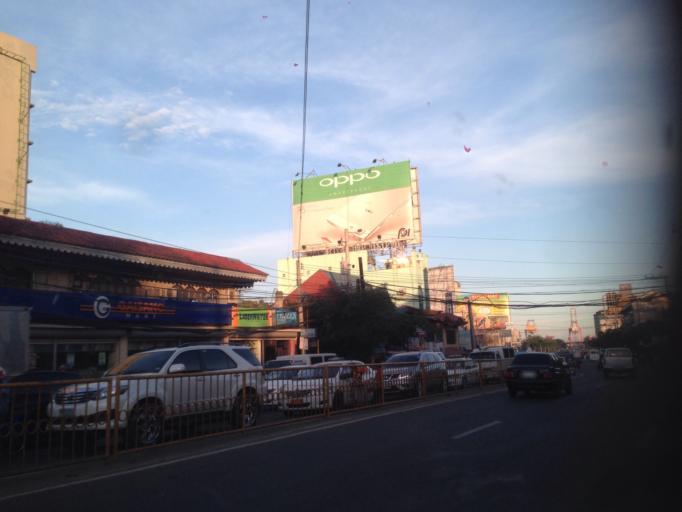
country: PH
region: Central Visayas
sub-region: Cebu City
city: Baugo
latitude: 10.3141
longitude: 123.9147
